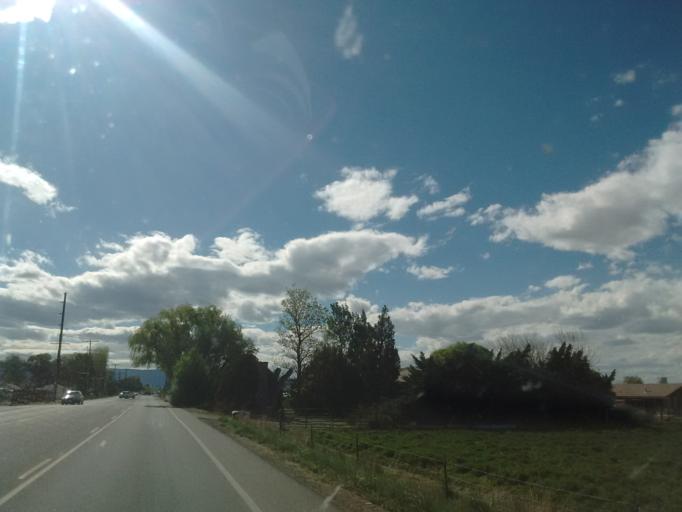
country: US
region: Colorado
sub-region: Mesa County
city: Fruitvale
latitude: 39.0629
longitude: -108.5097
